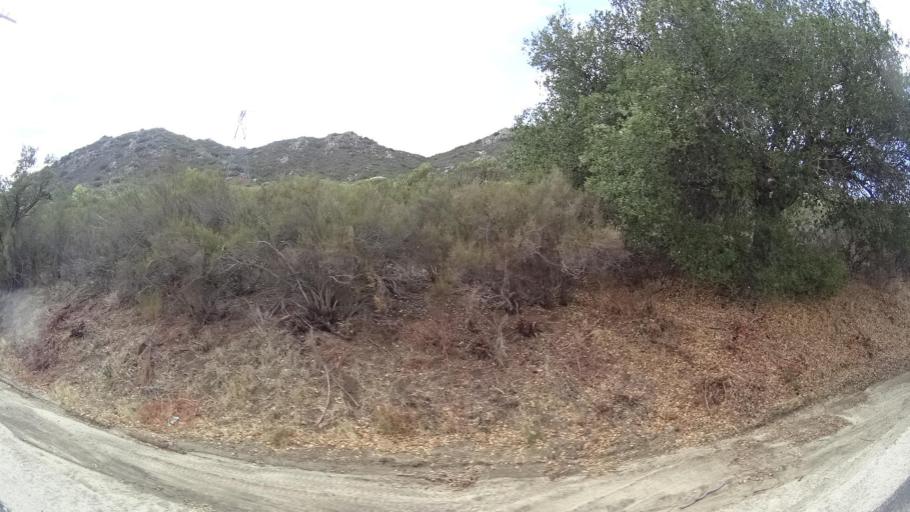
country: US
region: California
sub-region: San Diego County
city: Campo
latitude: 32.6591
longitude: -116.4878
